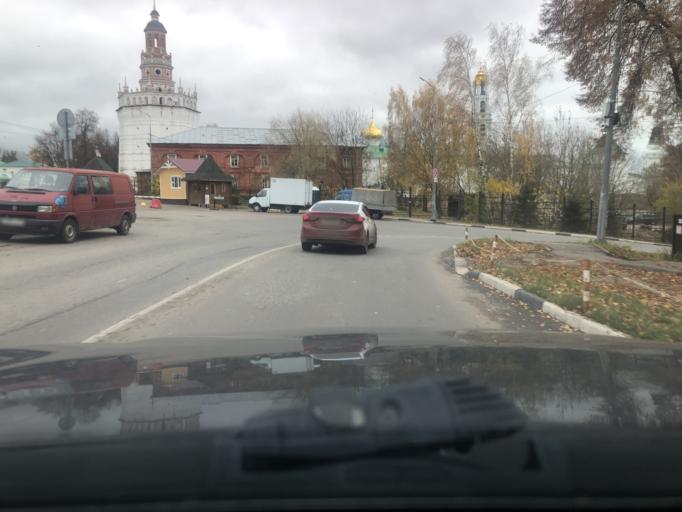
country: RU
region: Moskovskaya
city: Sergiyev Posad
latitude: 56.3139
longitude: 38.1315
